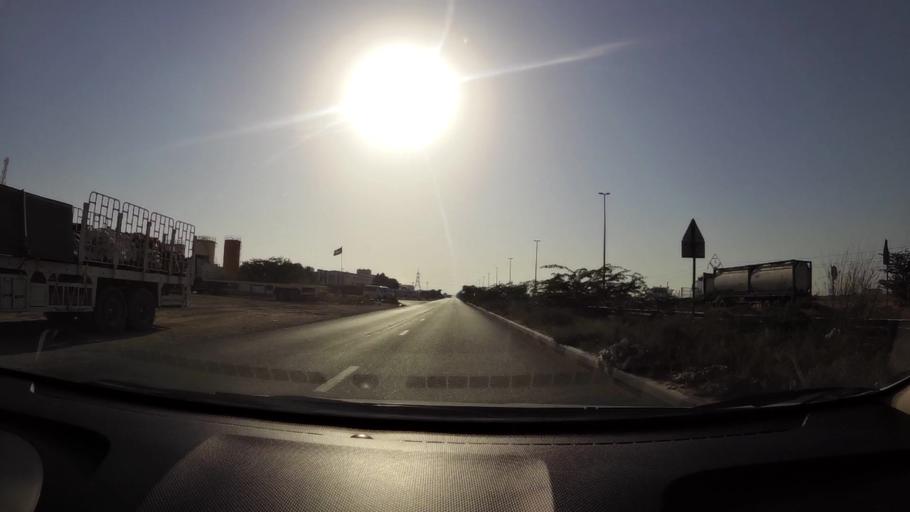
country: AE
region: Ajman
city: Ajman
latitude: 25.4425
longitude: 55.5467
